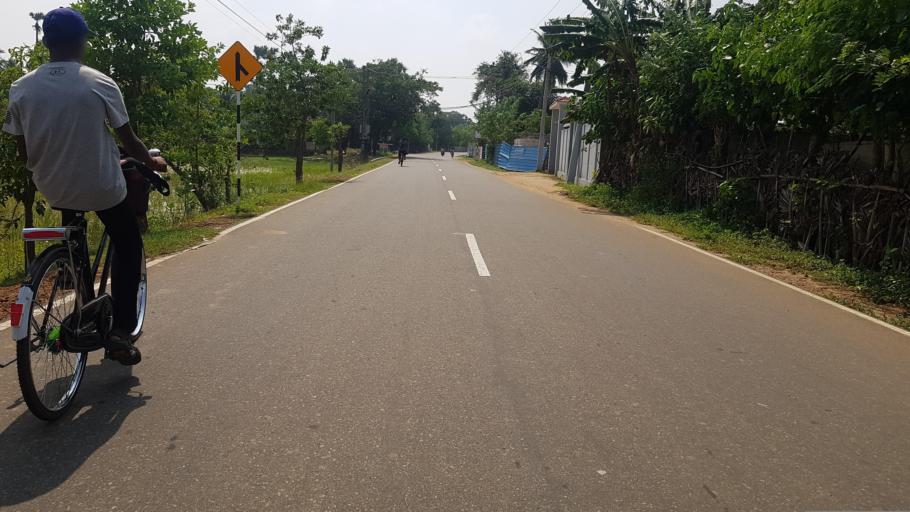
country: LK
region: Northern Province
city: Jaffna
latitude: 9.7245
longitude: 79.9471
